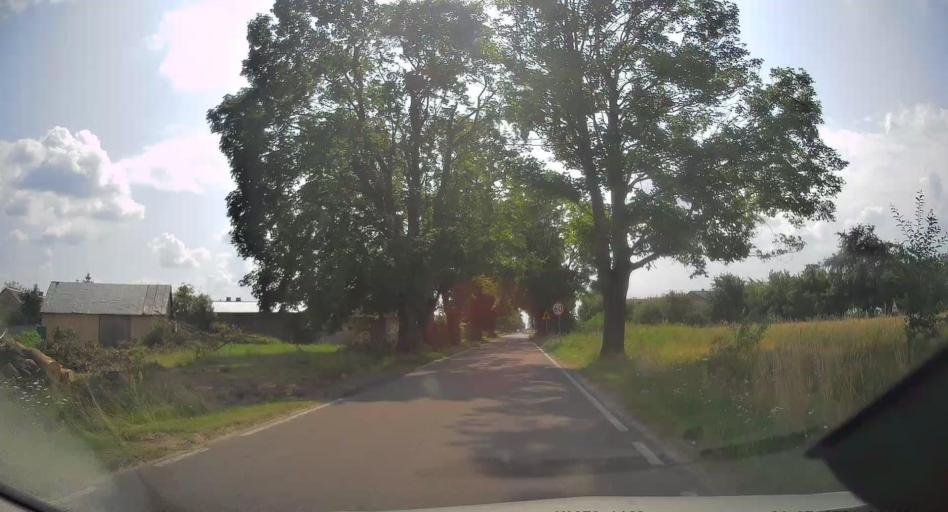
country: PL
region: Lodz Voivodeship
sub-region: Powiat tomaszowski
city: Lubochnia
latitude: 51.5739
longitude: 20.0956
